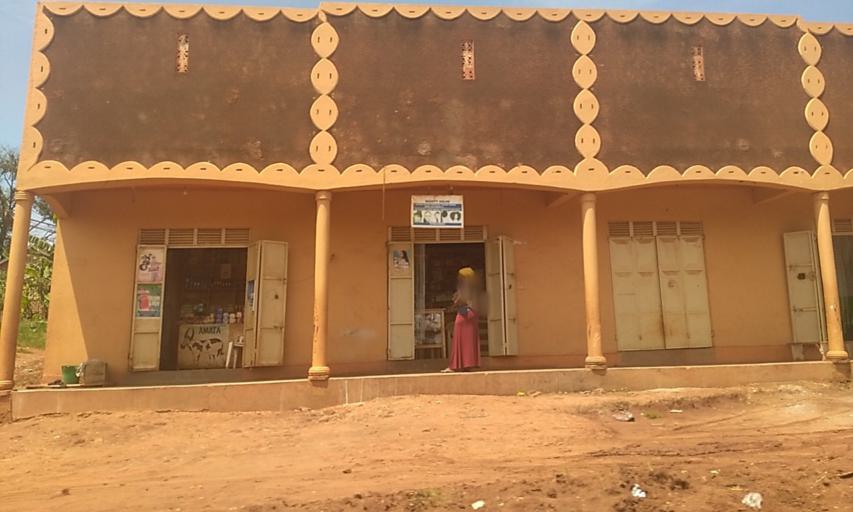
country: UG
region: Central Region
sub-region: Wakiso District
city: Wakiso
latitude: 0.4007
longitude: 32.4850
